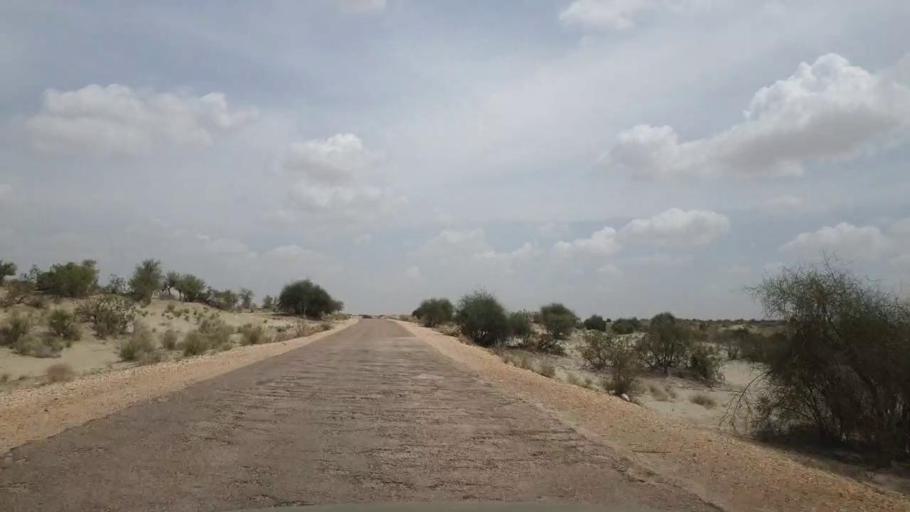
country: PK
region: Sindh
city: Kot Diji
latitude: 27.1792
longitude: 69.1862
